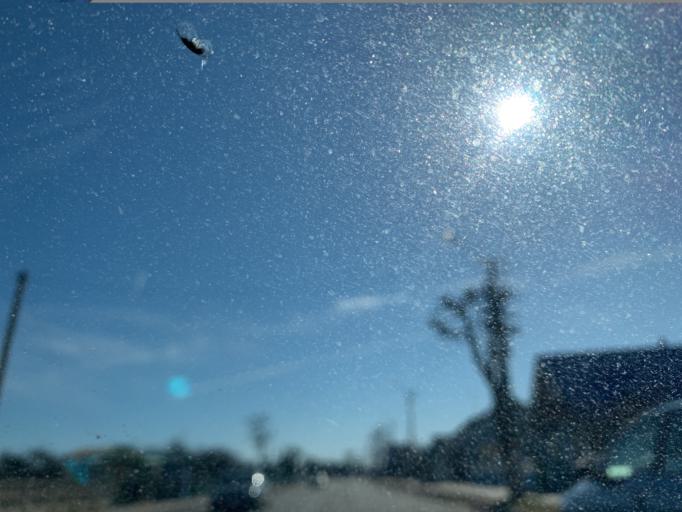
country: BY
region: Minsk
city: Nyasvizh
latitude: 53.2143
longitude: 26.6932
